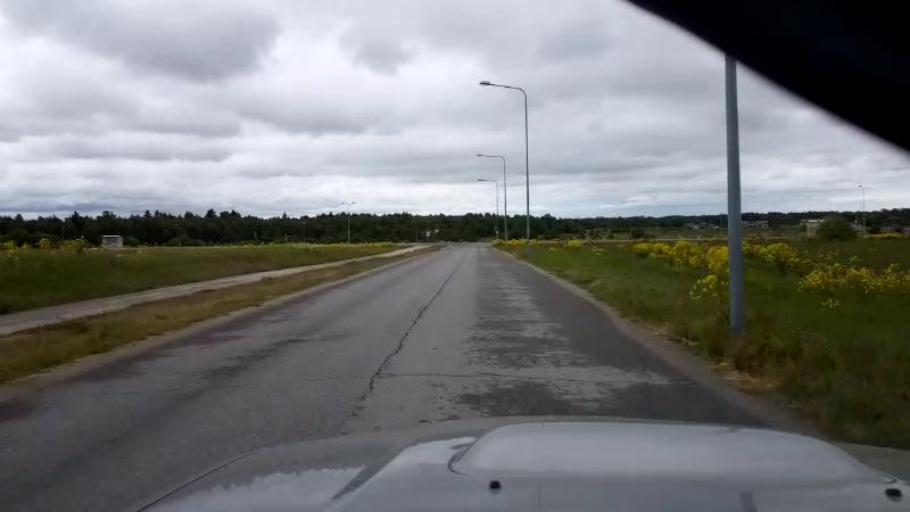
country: EE
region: Harju
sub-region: Harku vald
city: Tabasalu
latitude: 59.4534
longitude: 24.4563
